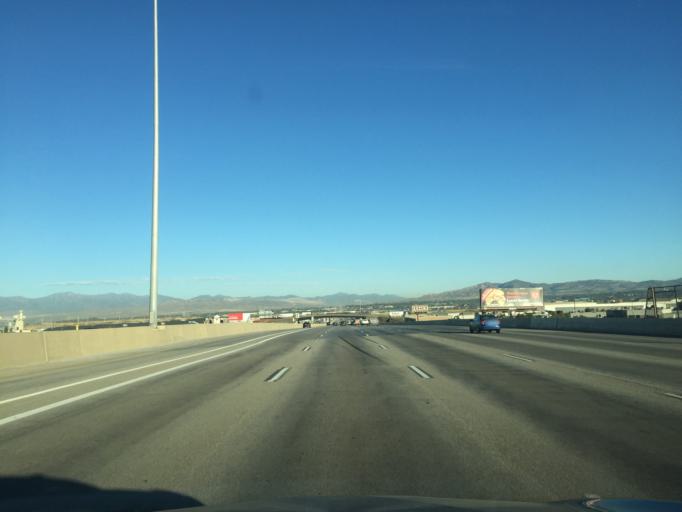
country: US
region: Utah
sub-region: Utah County
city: Lindon
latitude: 40.3305
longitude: -111.7383
